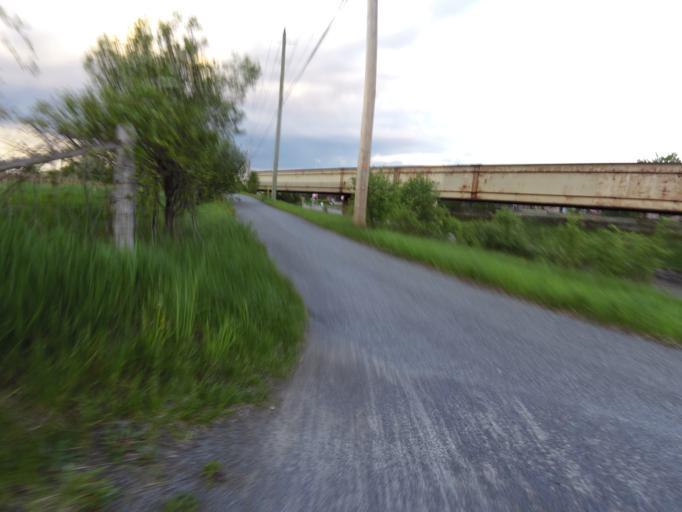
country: CA
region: Ontario
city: Bells Corners
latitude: 45.3171
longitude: -75.8459
